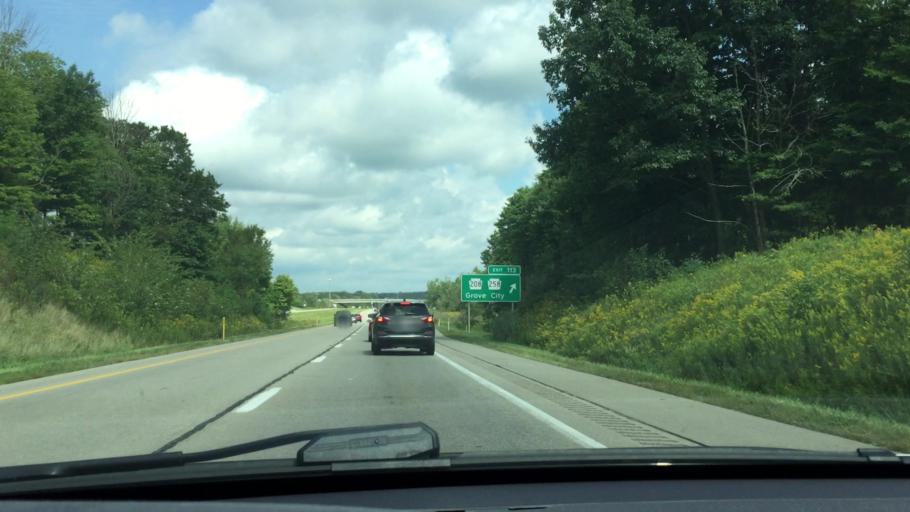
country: US
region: Pennsylvania
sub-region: Mercer County
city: Grove City
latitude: 41.1364
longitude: -80.1535
